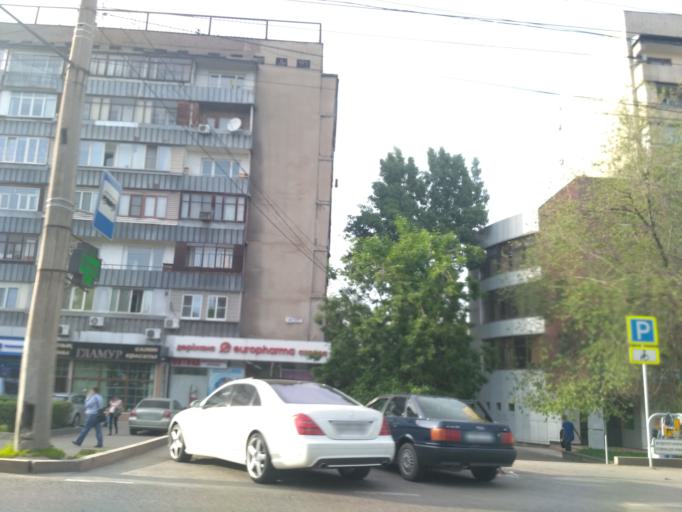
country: KZ
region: Almaty Qalasy
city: Almaty
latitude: 43.2393
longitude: 76.8980
